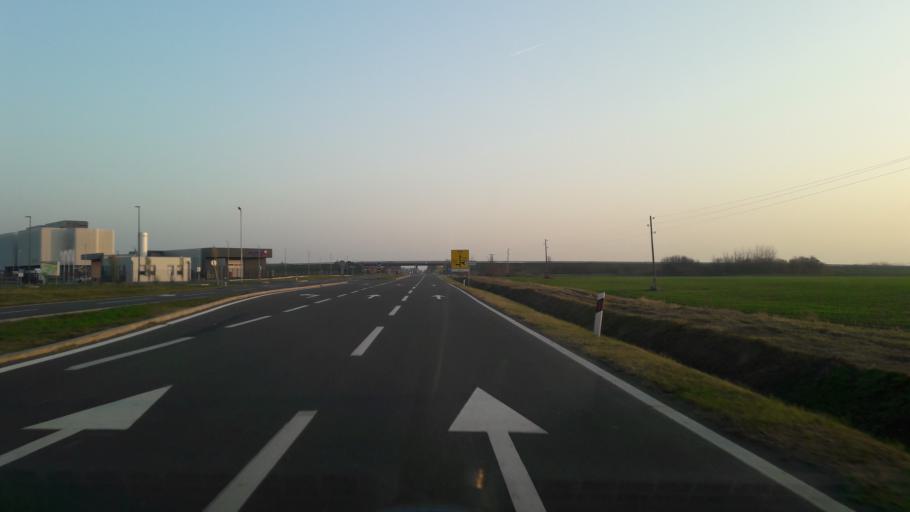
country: HR
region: Osjecko-Baranjska
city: Tenja
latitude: 45.5283
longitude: 18.7744
